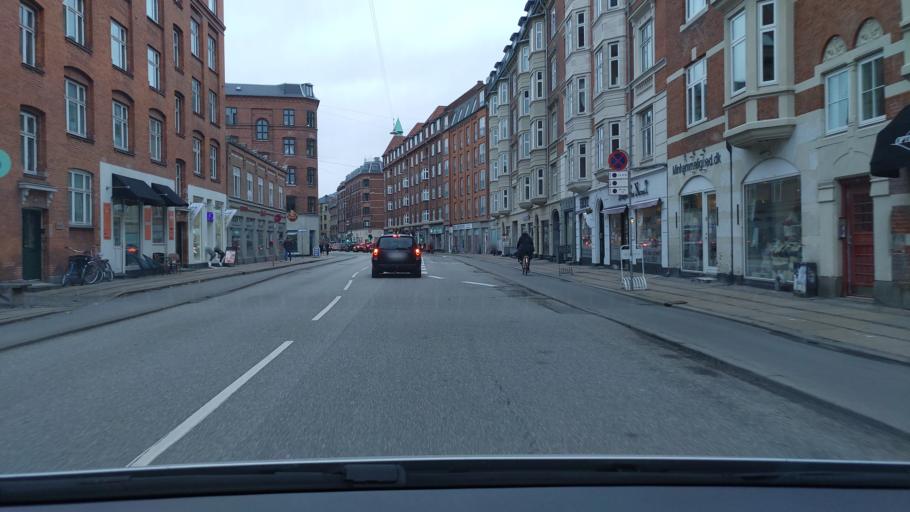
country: DK
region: Capital Region
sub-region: Kobenhavn
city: Christianshavn
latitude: 55.6569
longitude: 12.6090
